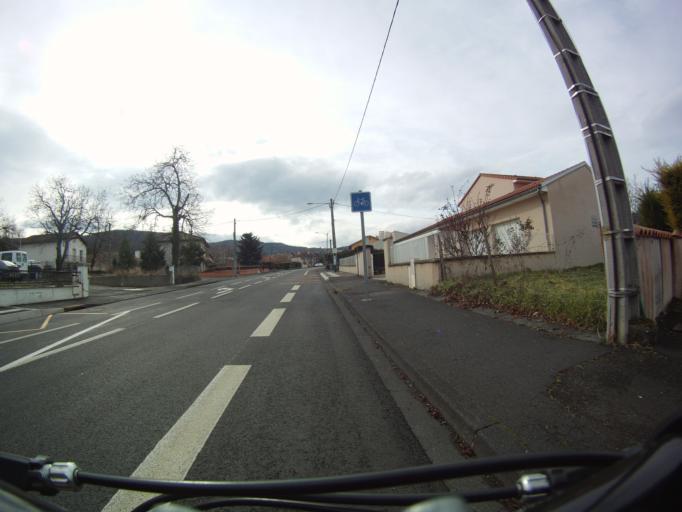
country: FR
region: Auvergne
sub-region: Departement du Puy-de-Dome
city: Romagnat
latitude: 45.7398
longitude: 3.1063
